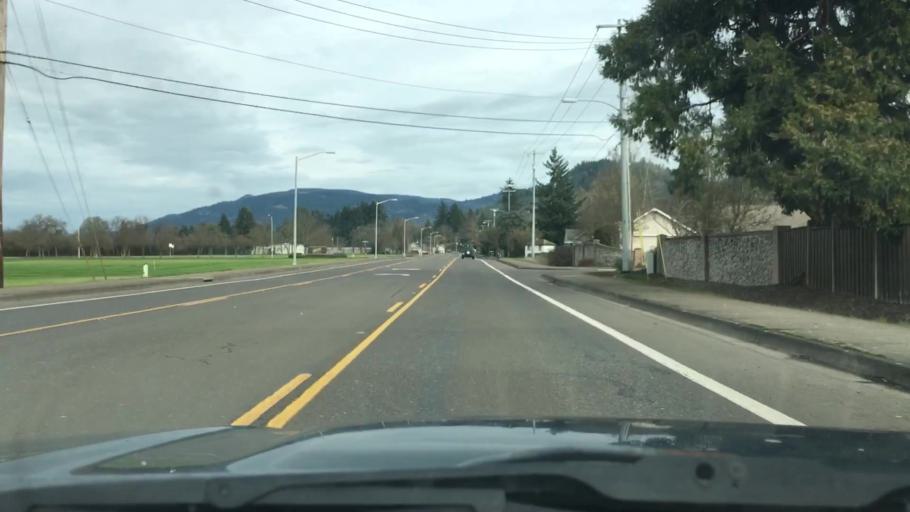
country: US
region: Oregon
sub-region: Lane County
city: Coburg
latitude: 44.1009
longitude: -123.0622
